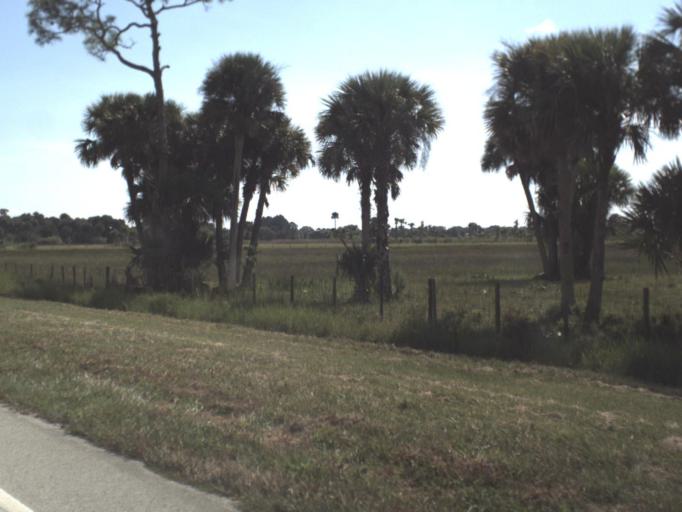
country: US
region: Florida
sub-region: Okeechobee County
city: Okeechobee
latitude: 27.2815
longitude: -80.8783
